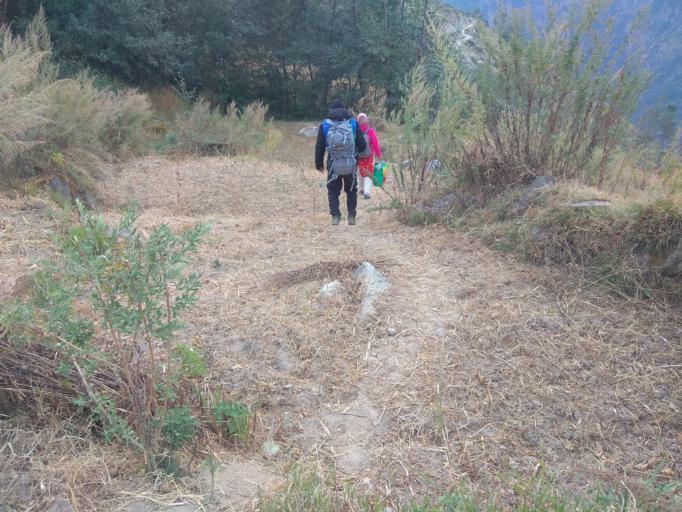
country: NP
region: Far Western
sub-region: Seti Zone
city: Achham
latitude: 29.2321
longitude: 81.6437
